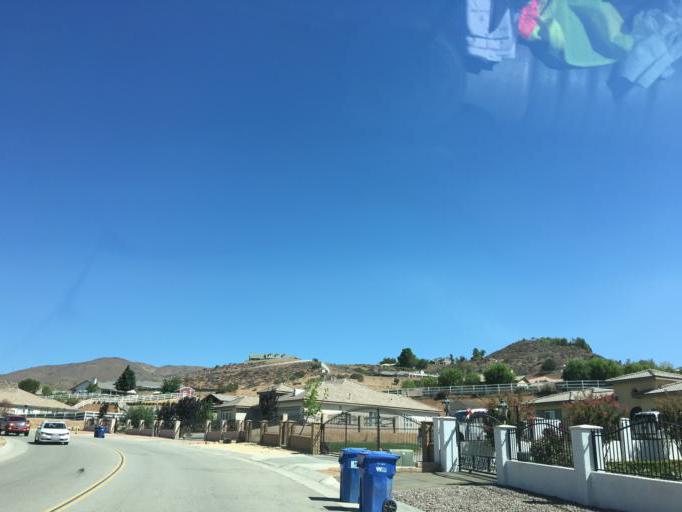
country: US
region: California
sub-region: Los Angeles County
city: Acton
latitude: 34.4937
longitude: -118.1641
